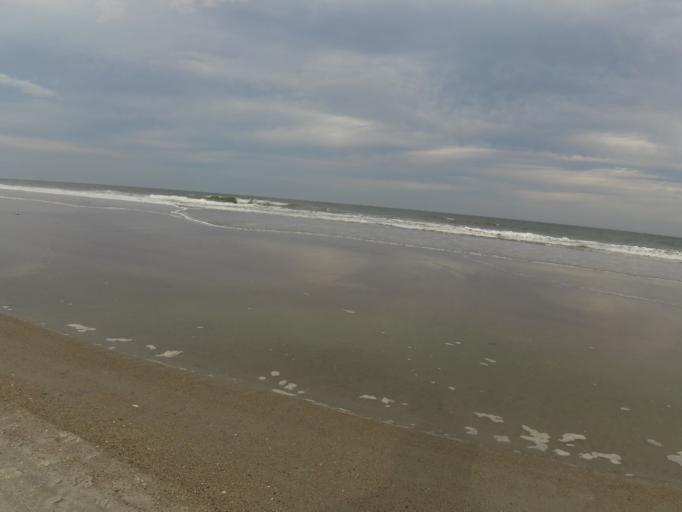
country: US
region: Florida
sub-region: Duval County
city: Neptune Beach
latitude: 30.3219
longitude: -81.3938
